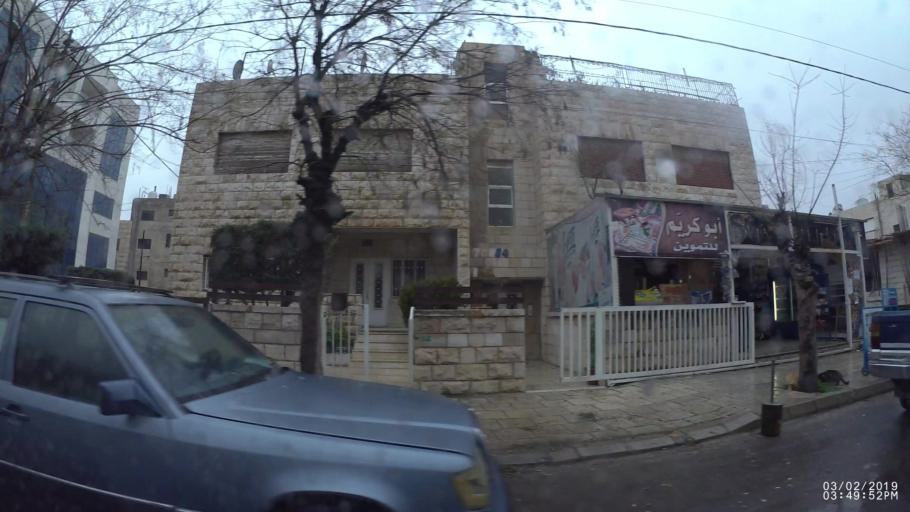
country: JO
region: Amman
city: Amman
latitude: 31.9752
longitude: 35.9130
